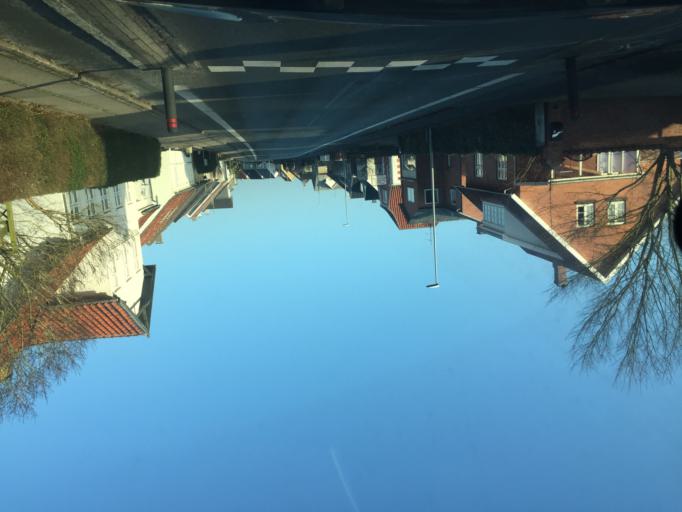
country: DK
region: South Denmark
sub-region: Faaborg-Midtfyn Kommune
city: Faaborg
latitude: 55.1024
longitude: 10.2287
